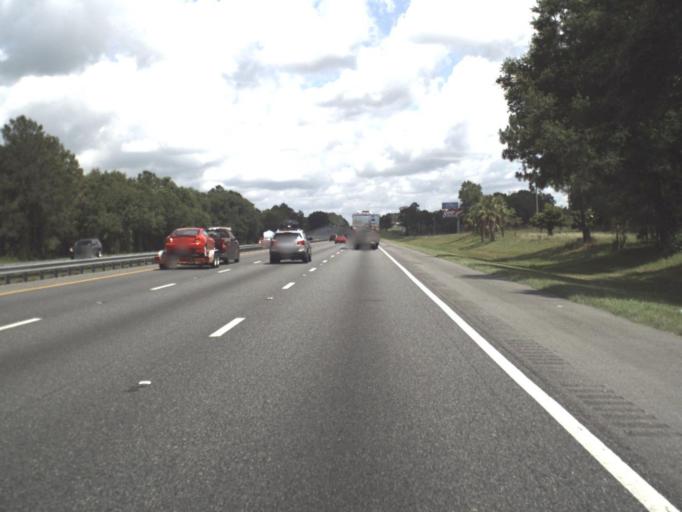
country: US
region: Florida
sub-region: Columbia County
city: Lake City
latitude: 30.1393
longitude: -82.6677
